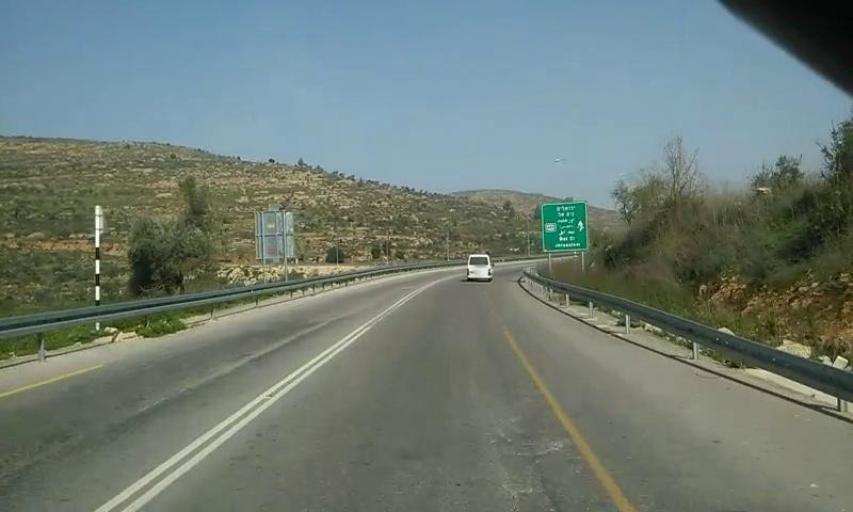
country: PS
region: West Bank
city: `Atarah
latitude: 31.9877
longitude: 35.2273
